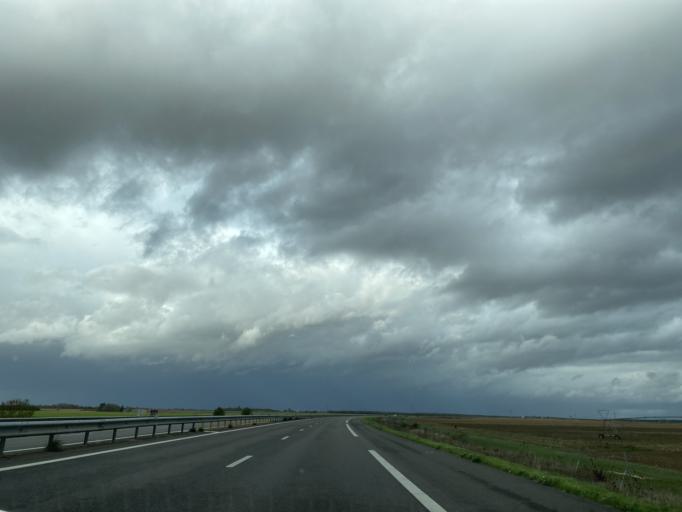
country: FR
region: Centre
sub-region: Departement du Cher
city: Levet
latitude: 46.9450
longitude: 2.4166
